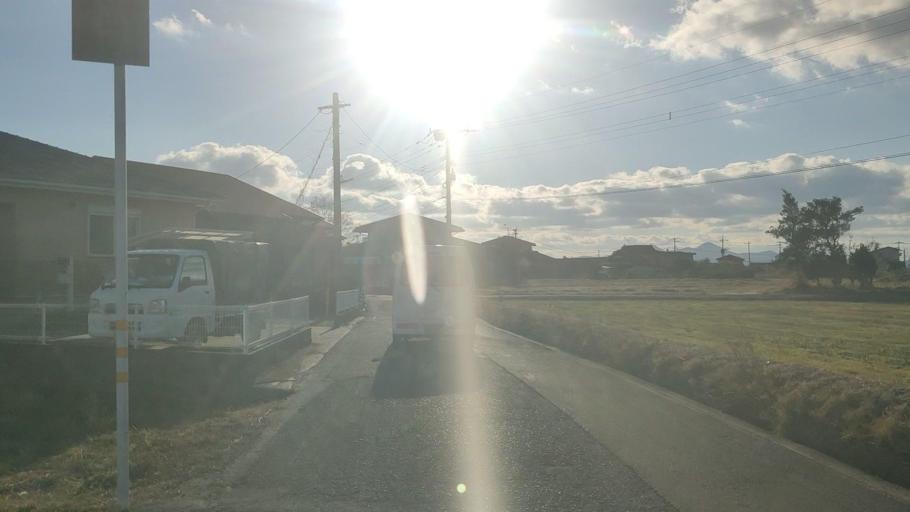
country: JP
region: Saga Prefecture
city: Saga-shi
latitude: 33.2950
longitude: 130.2421
